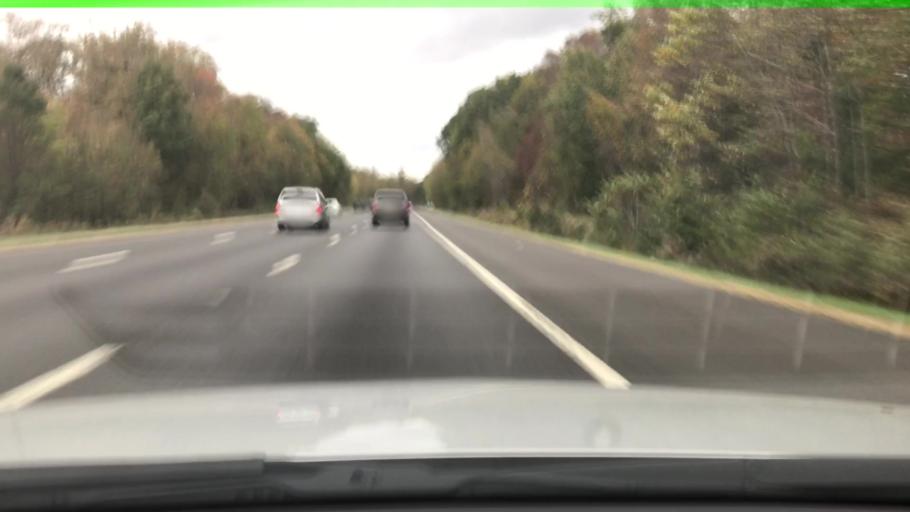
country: US
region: New Jersey
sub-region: Burlington County
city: Roebling
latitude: 40.0675
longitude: -74.7917
